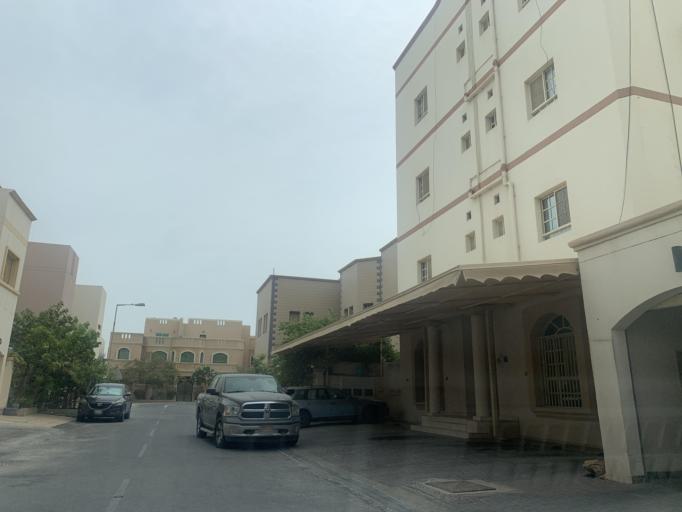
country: BH
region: Muharraq
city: Al Hadd
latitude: 26.2787
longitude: 50.6409
